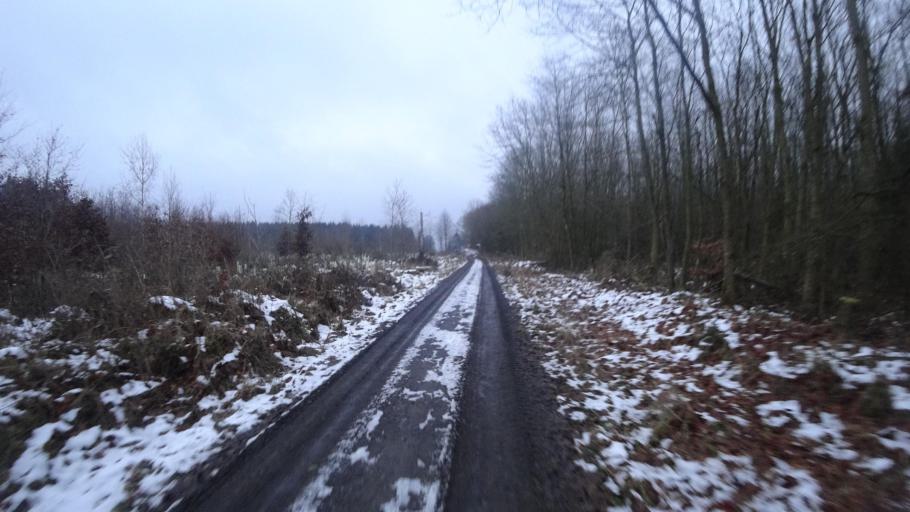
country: DE
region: Rheinland-Pfalz
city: Ailertchen
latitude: 50.6081
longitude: 7.9200
